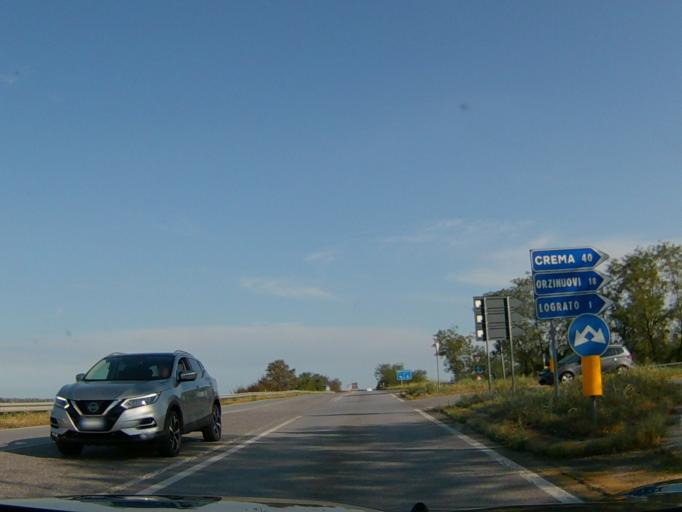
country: IT
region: Lombardy
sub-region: Provincia di Brescia
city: Travagliato
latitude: 45.4980
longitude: 10.0812
